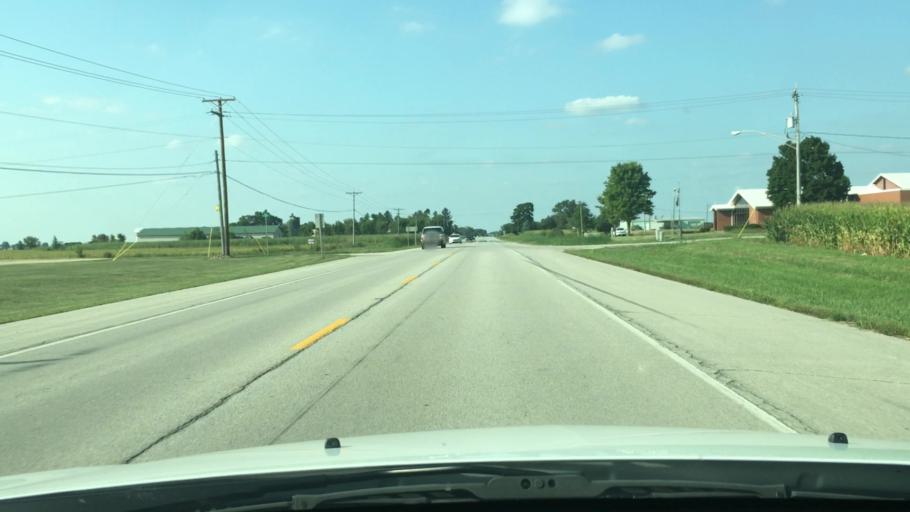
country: US
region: Illinois
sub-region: DeKalb County
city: DeKalb
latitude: 41.8777
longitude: -88.7538
